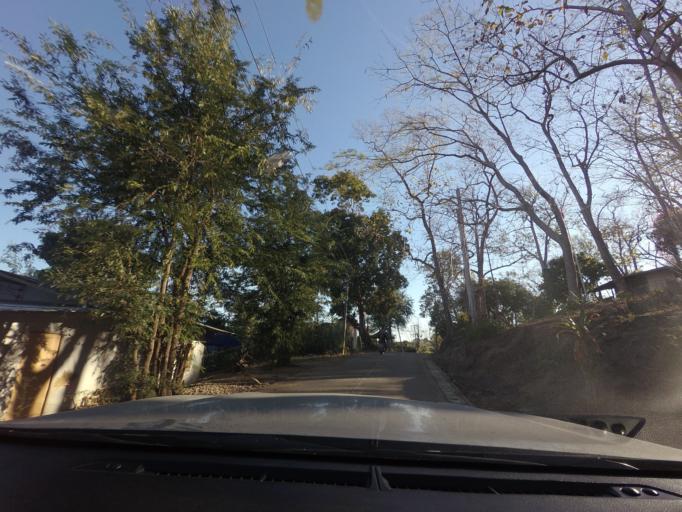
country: TH
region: Mae Hong Son
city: Wiang Nuea
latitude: 19.3985
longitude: 98.4217
